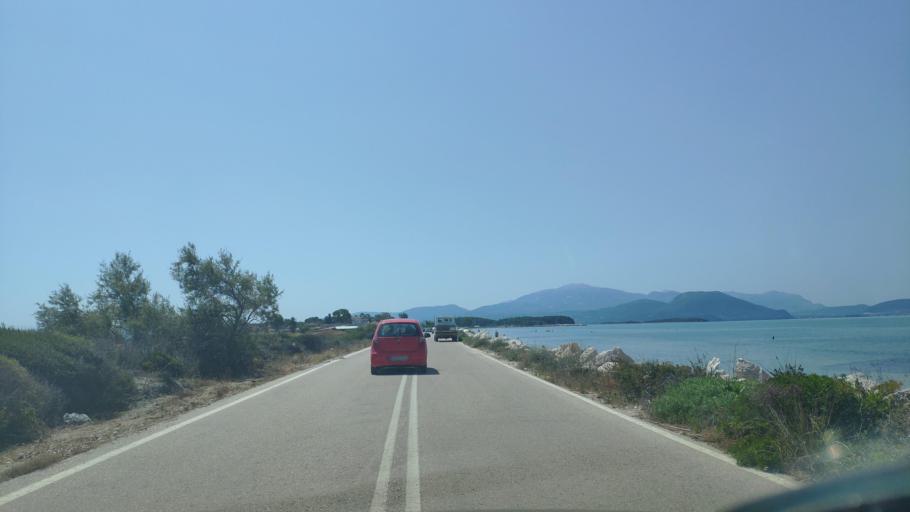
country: GR
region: Epirus
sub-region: Nomos Artas
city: Aneza
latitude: 39.0228
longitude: 20.9096
